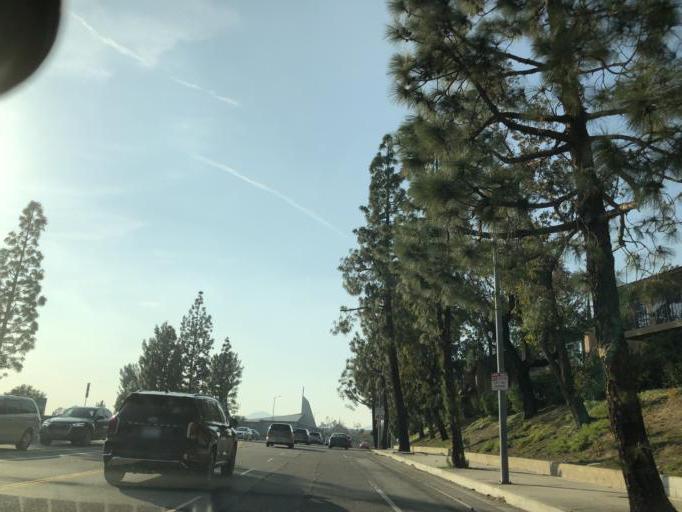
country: US
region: California
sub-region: Los Angeles County
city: Chatsworth
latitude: 34.2747
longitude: -118.5571
